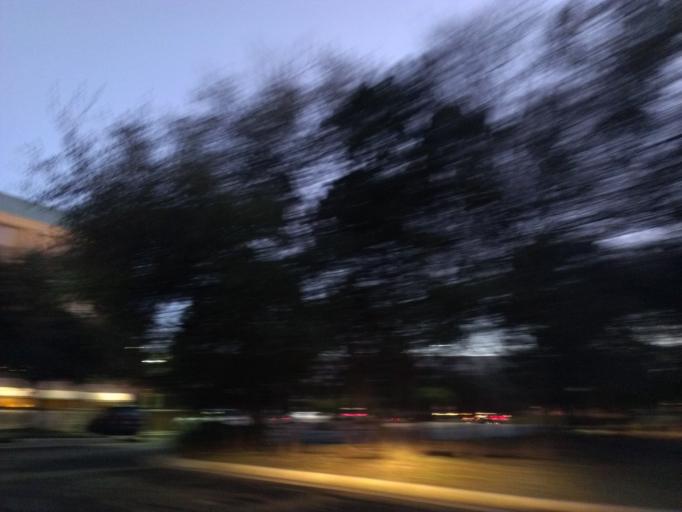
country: US
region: Texas
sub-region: Williamson County
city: Jollyville
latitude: 30.3977
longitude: -97.7351
